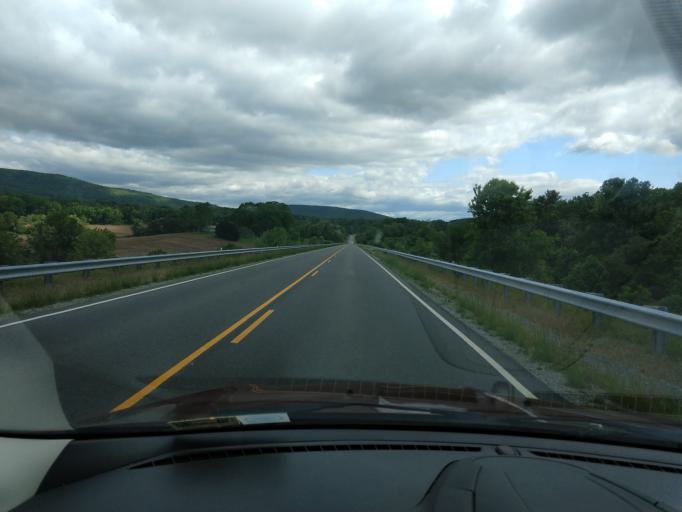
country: US
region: Virginia
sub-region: Wythe County
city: Wytheville
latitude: 36.8816
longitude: -80.9806
